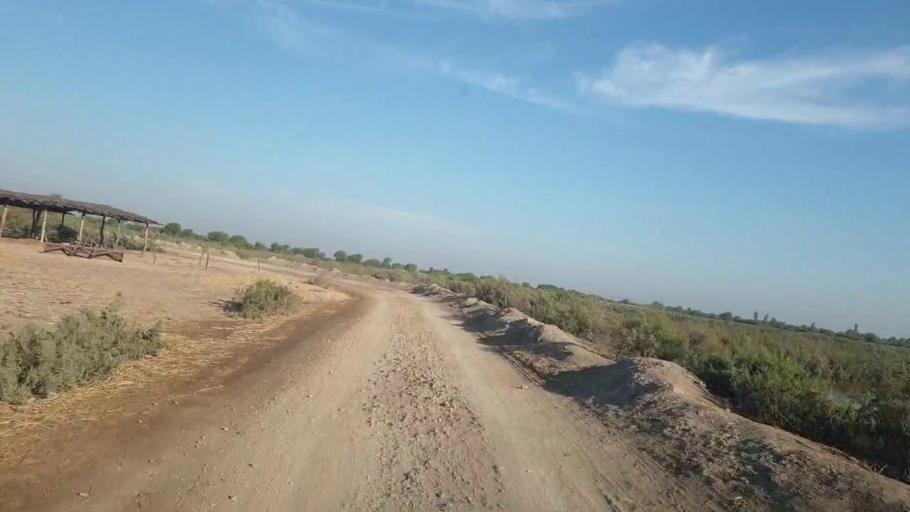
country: PK
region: Sindh
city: Talhar
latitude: 24.8180
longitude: 68.8396
